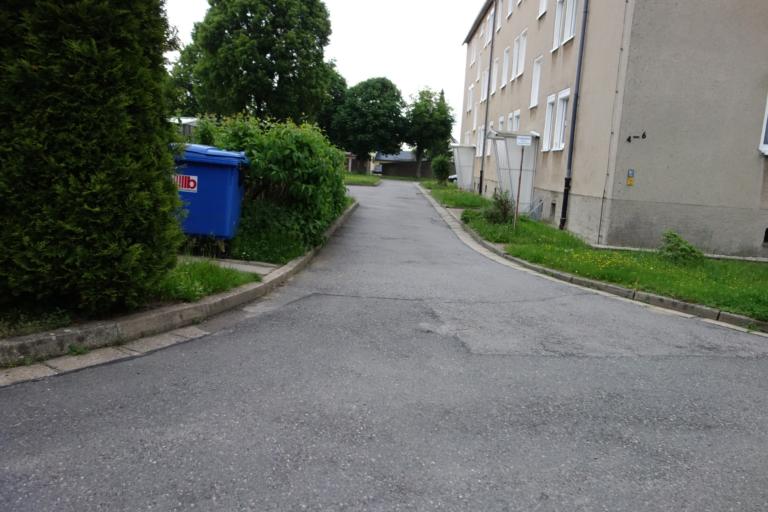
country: DE
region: Saxony
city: Freiberg
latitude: 50.8909
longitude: 13.3472
